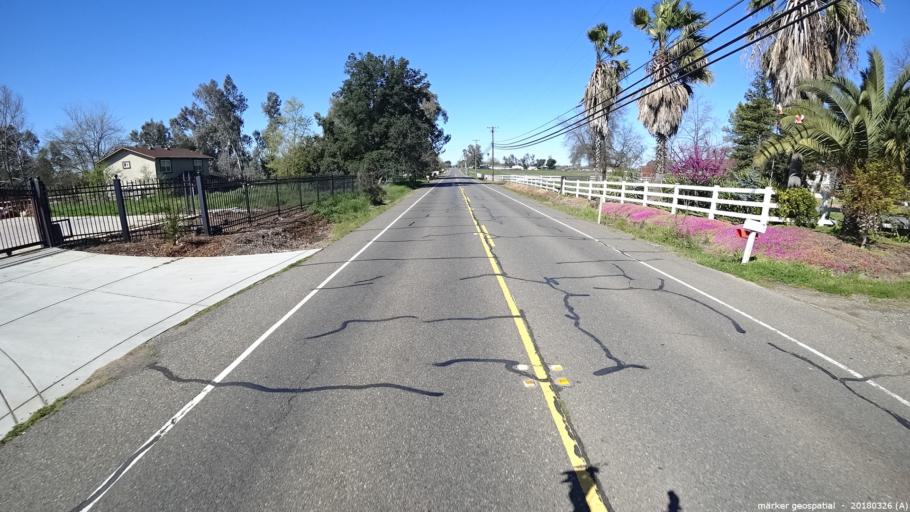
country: US
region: California
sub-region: Sacramento County
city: Wilton
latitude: 38.4526
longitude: -121.2844
